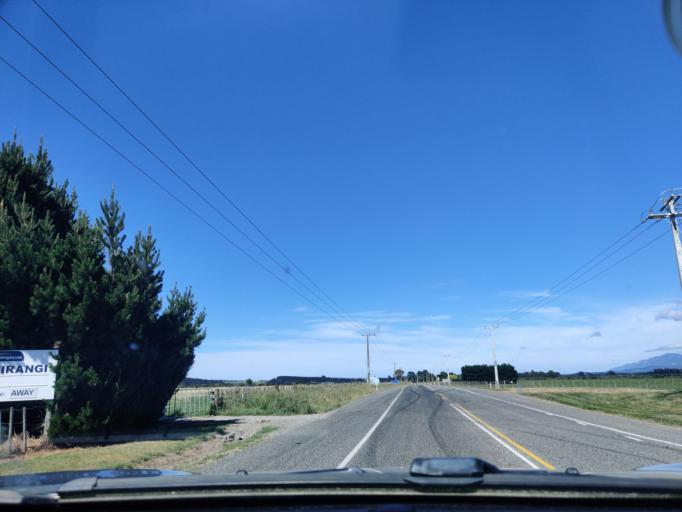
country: NZ
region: Wellington
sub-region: South Wairarapa District
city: Waipawa
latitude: -41.3061
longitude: 175.2735
